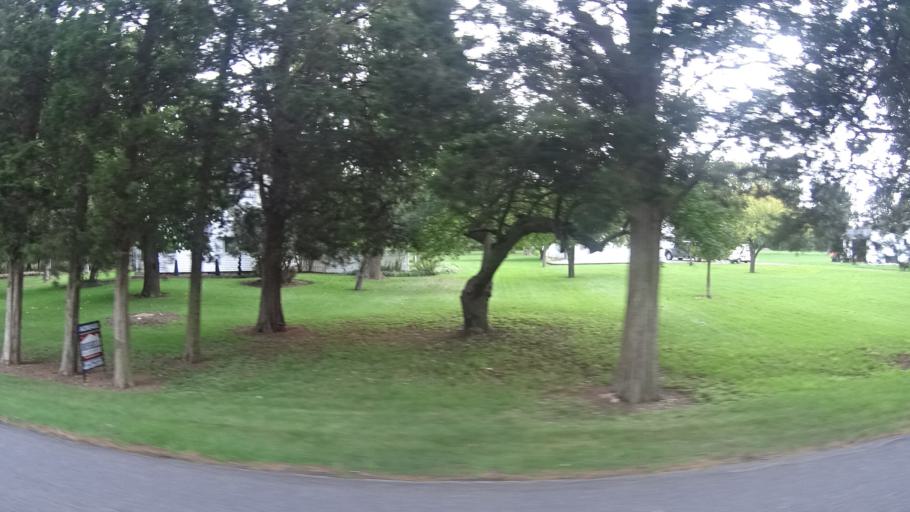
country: US
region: Ohio
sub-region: Erie County
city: Sandusky
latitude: 41.6031
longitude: -82.7090
